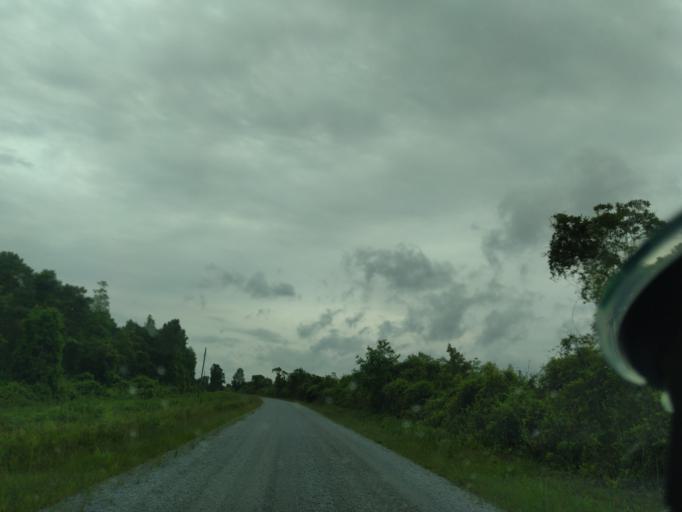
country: US
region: North Carolina
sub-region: Beaufort County
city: Belhaven
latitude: 35.7334
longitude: -76.4497
